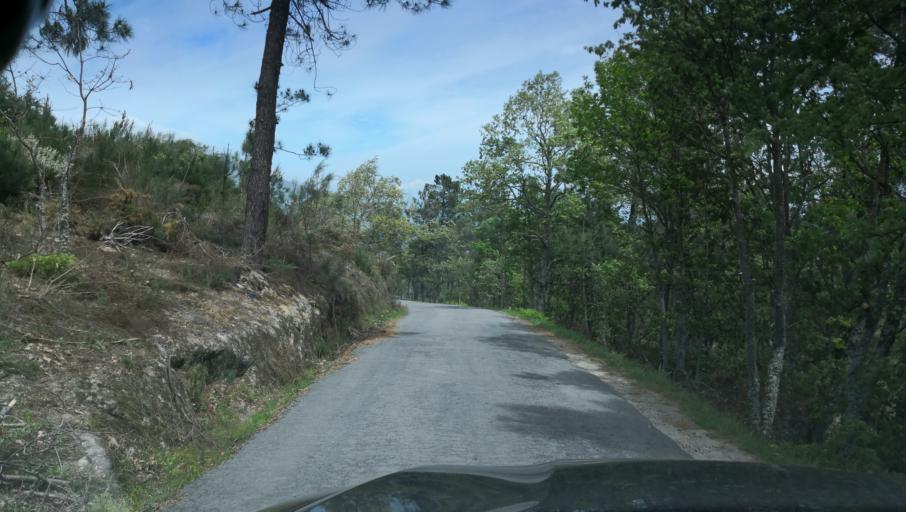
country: PT
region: Vila Real
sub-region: Vila Real
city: Vila Real
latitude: 41.2960
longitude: -7.8031
